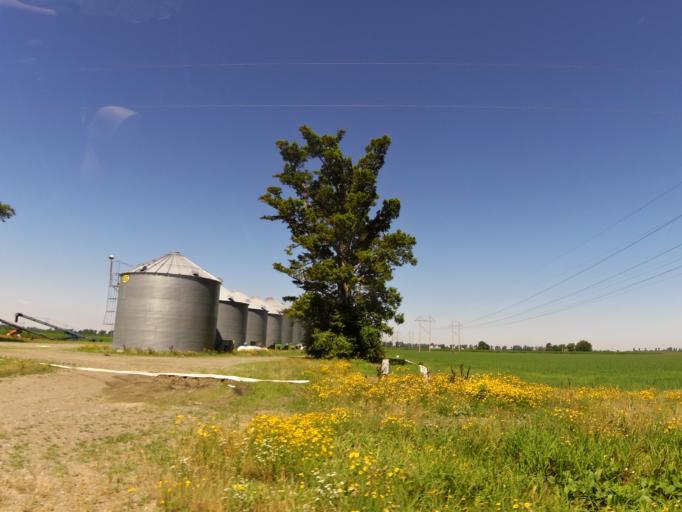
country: US
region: Missouri
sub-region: New Madrid County
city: Lilbourn
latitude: 36.5763
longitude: -89.7027
